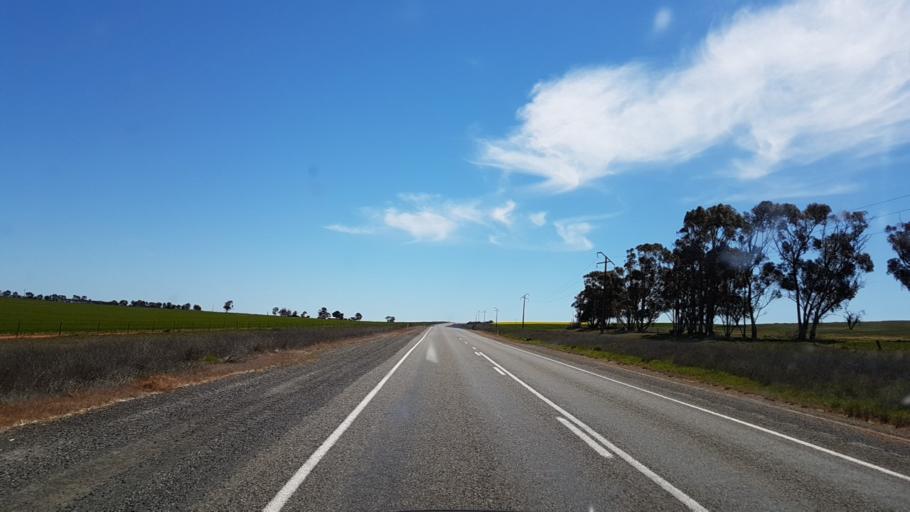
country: AU
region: South Australia
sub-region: Clare and Gilbert Valleys
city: Clare
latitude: -33.8150
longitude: 138.8471
